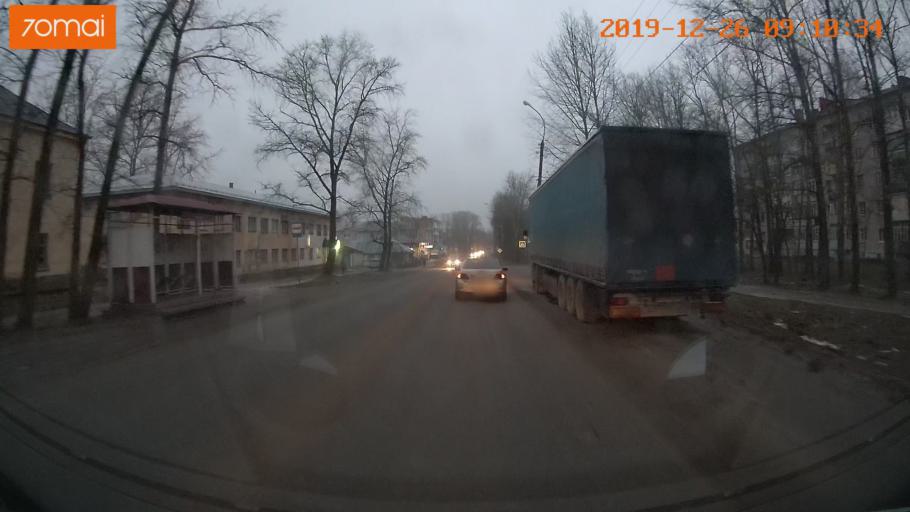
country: RU
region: Vologda
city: Gryazovets
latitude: 58.8718
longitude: 40.2526
